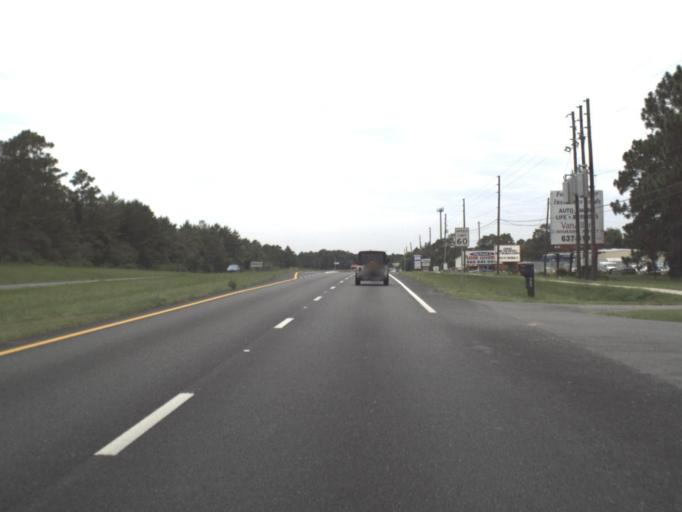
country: US
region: Florida
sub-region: Citrus County
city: Citrus Hills
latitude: 28.8576
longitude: -82.4211
